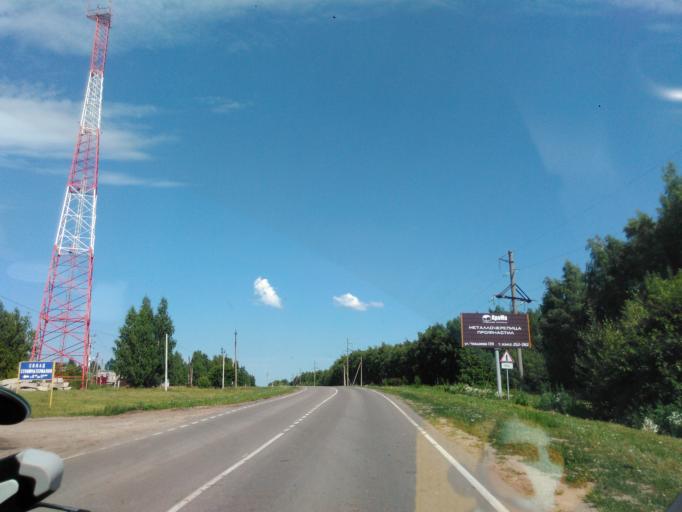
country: RU
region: Penza
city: Belinskiy
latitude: 52.9672
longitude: 43.4547
